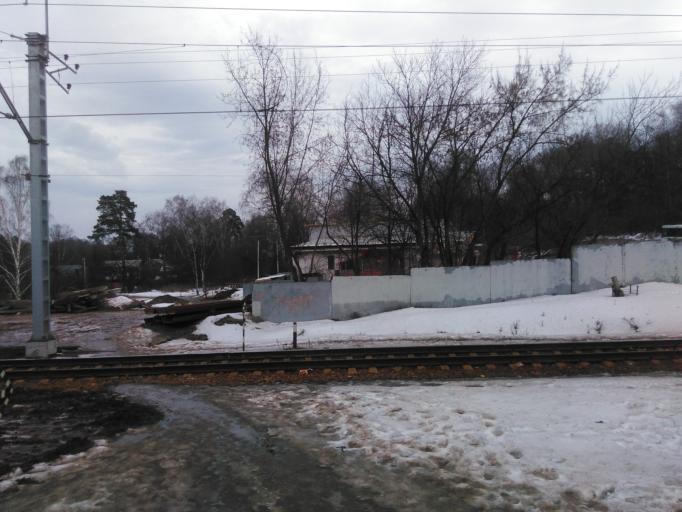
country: RU
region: Moskovskaya
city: Mamontovka
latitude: 55.9951
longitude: 37.8293
